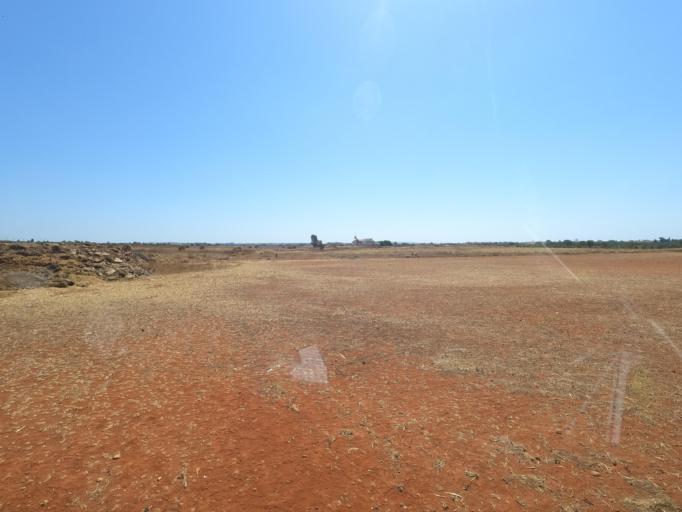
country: CY
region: Ammochostos
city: Liopetri
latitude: 35.0203
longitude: 33.8814
